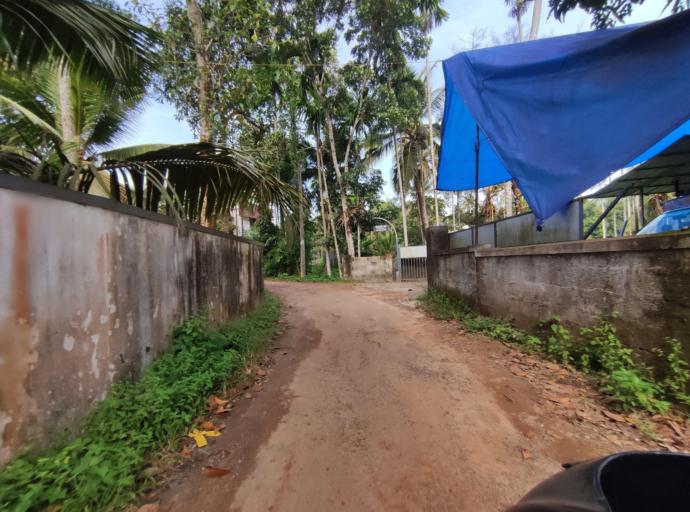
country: IN
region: Kerala
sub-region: Alappuzha
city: Vayalar
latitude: 9.7006
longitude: 76.3197
